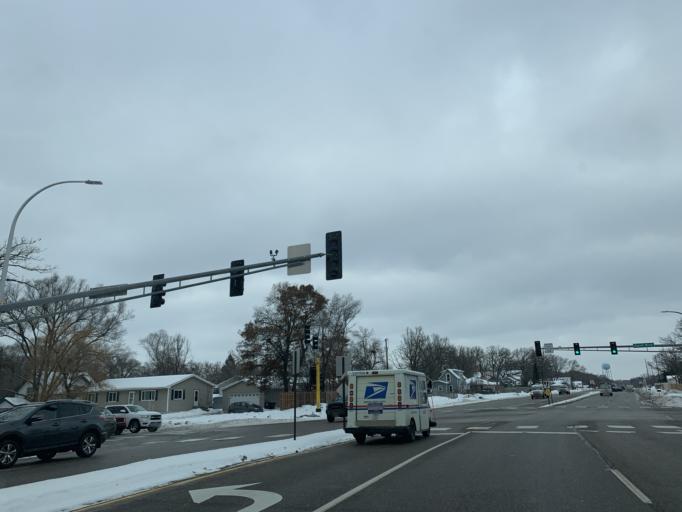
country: US
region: Minnesota
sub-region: Anoka County
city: Blaine
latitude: 45.1636
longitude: -93.2766
